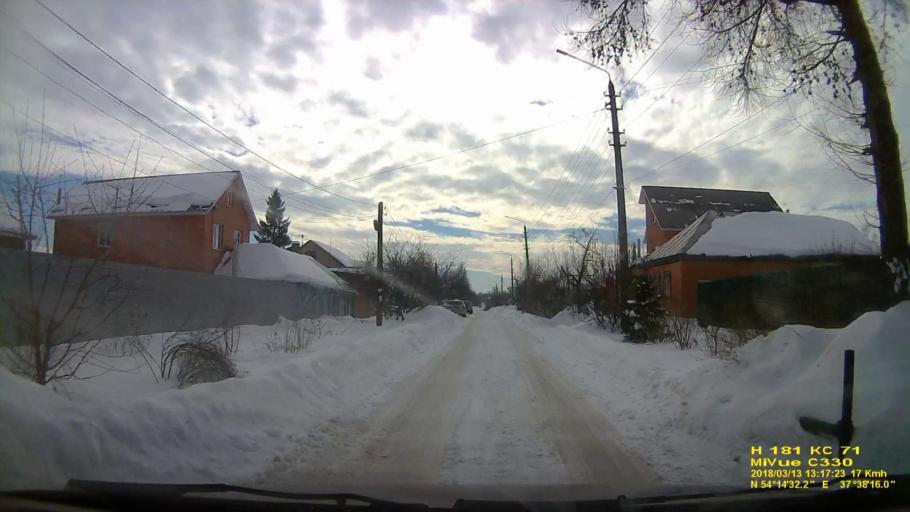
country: RU
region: Tula
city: Gorelki
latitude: 54.2422
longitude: 37.6377
